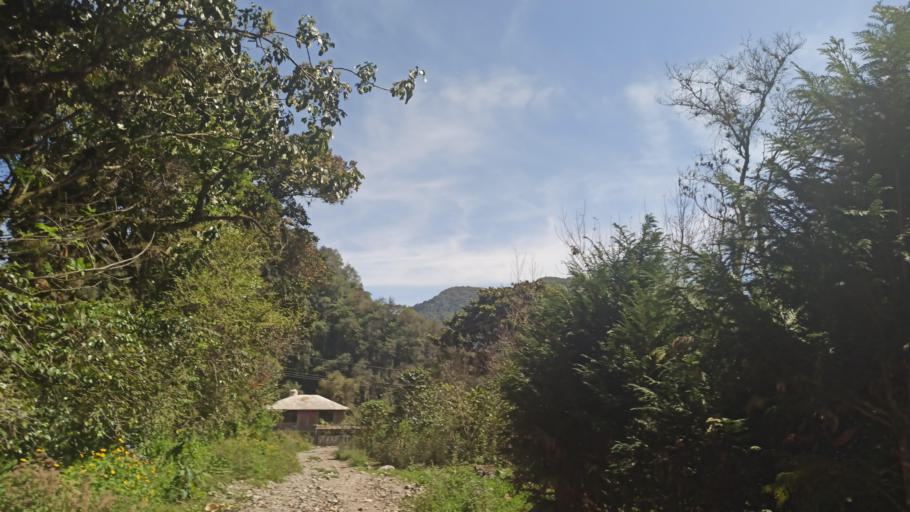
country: MX
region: Veracruz
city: Xocotla
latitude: 18.9799
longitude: -97.0889
